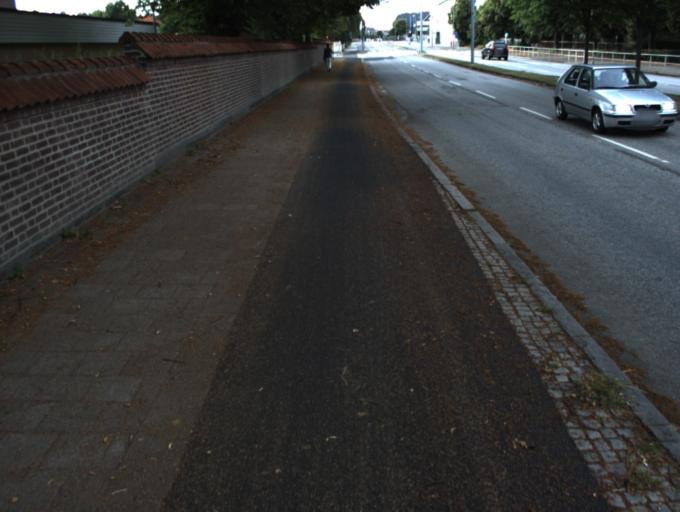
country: SE
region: Skane
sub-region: Helsingborg
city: Helsingborg
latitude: 56.0465
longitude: 12.7072
